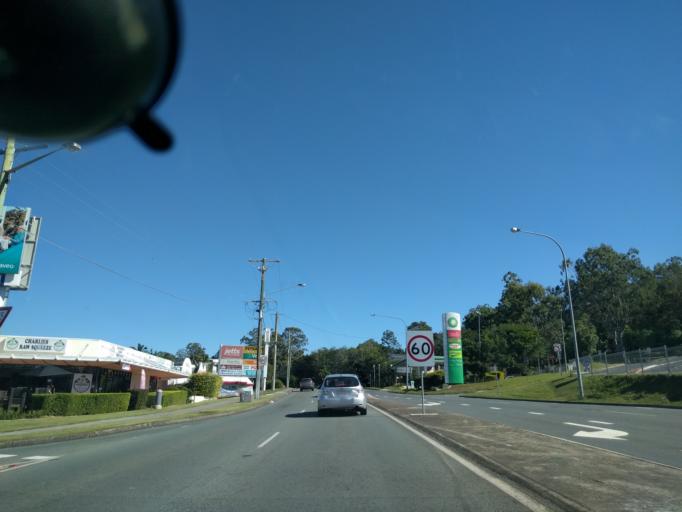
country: AU
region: Queensland
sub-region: Brisbane
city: Kenmore Hills
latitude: -27.5076
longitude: 152.9477
